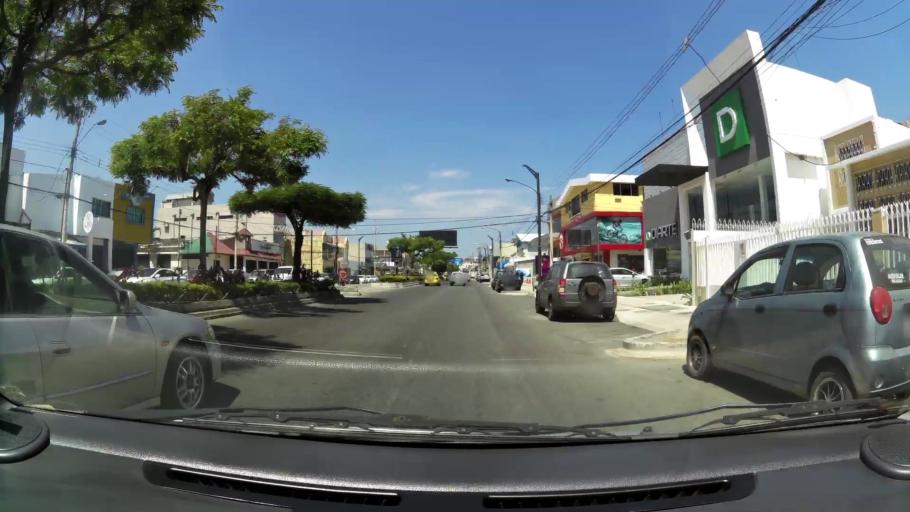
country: EC
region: Guayas
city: Guayaquil
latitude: -2.1667
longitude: -79.9112
